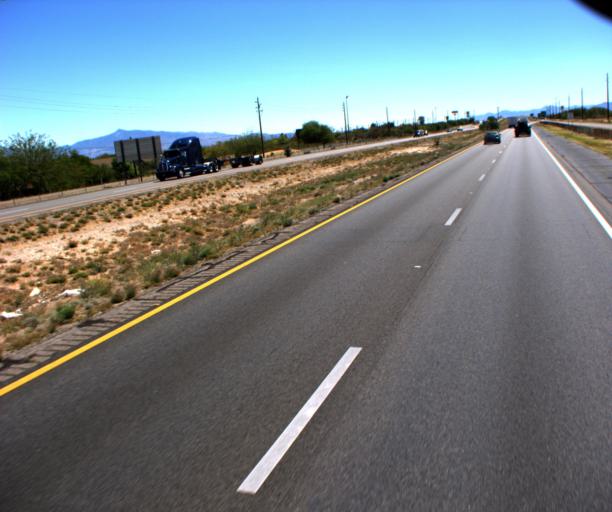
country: US
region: Arizona
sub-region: Pima County
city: Summit
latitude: 32.1201
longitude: -110.8671
